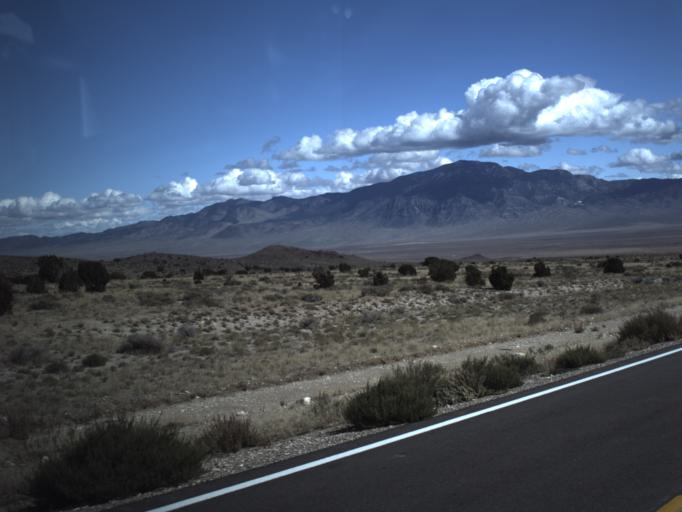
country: US
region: Utah
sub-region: Beaver County
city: Milford
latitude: 38.5010
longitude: -113.5009
